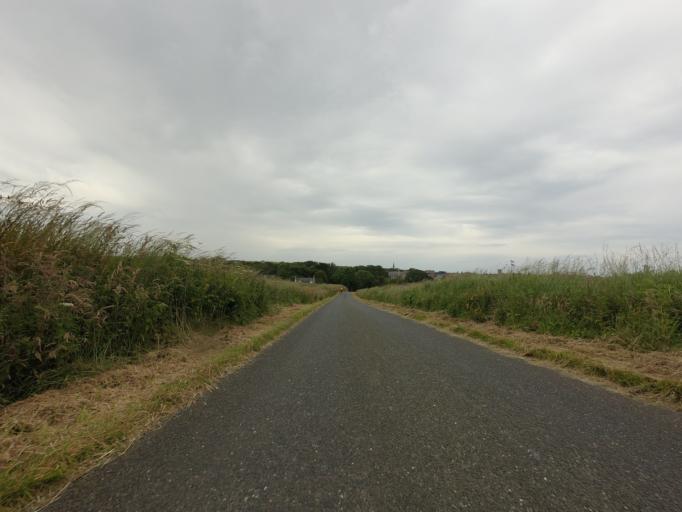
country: GB
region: Scotland
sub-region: Aberdeenshire
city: Portsoy
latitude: 57.6780
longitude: -2.6843
